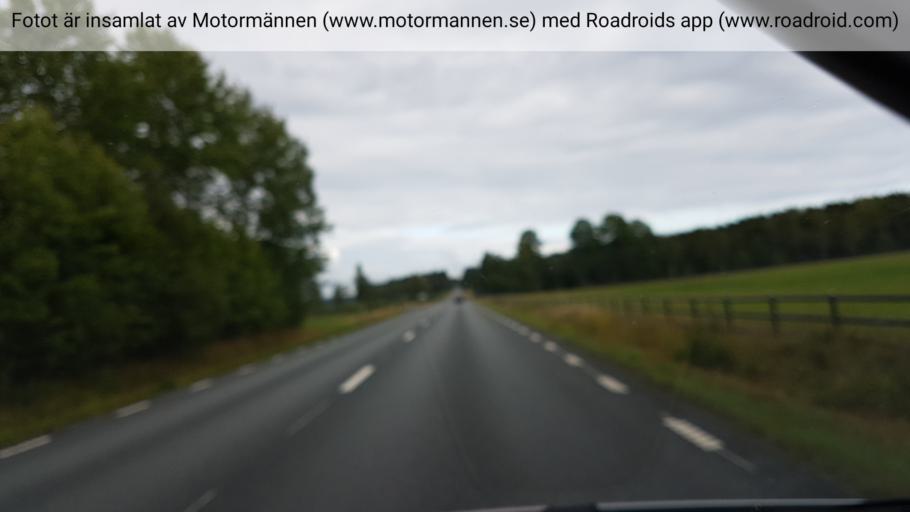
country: SE
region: Vaestra Goetaland
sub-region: Tidaholms Kommun
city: Olofstorp
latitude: 58.2027
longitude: 14.0512
